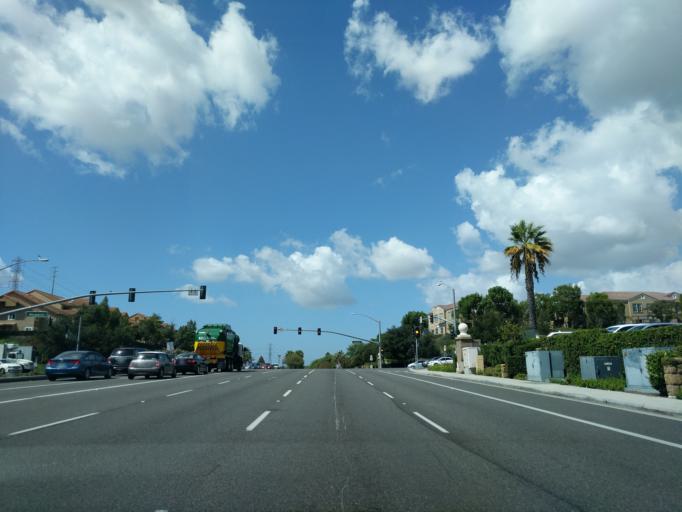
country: US
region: California
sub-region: Orange County
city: Ladera Ranch
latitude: 33.5634
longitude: -117.6573
